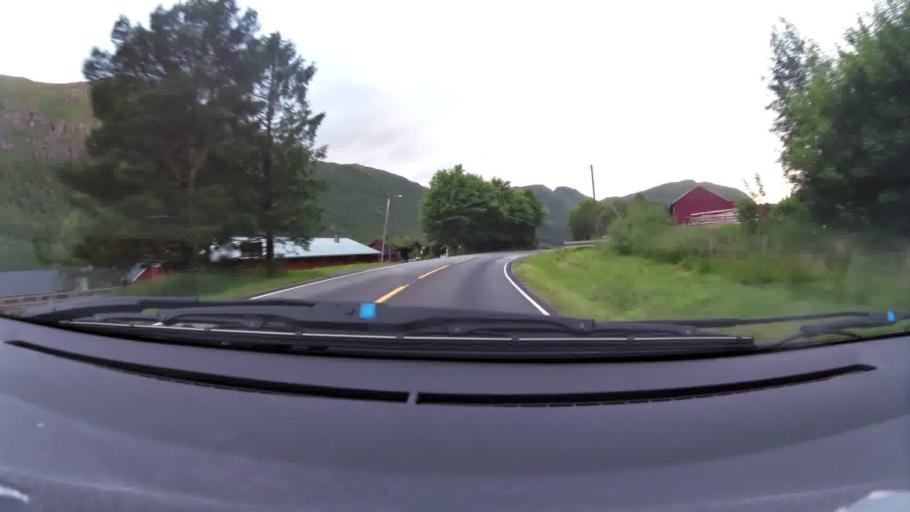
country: NO
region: More og Romsdal
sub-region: Molde
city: Molde
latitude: 62.7936
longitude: 7.2608
